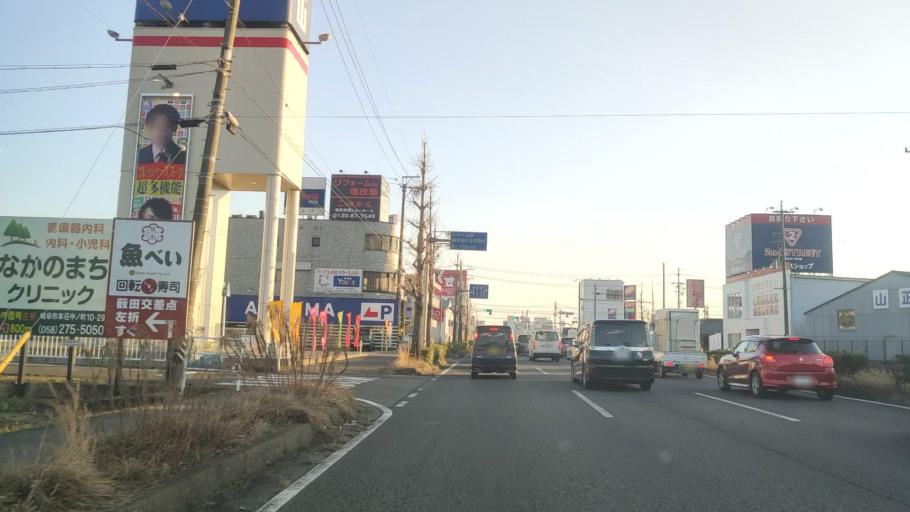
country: JP
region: Gifu
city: Gifu-shi
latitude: 35.4033
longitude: 136.7267
